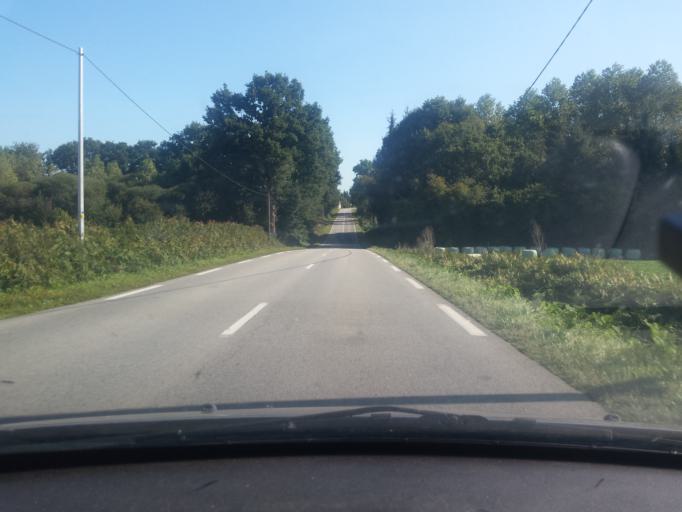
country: FR
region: Brittany
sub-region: Departement du Morbihan
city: Saint-Thuriau
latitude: 48.0231
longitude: -2.9121
